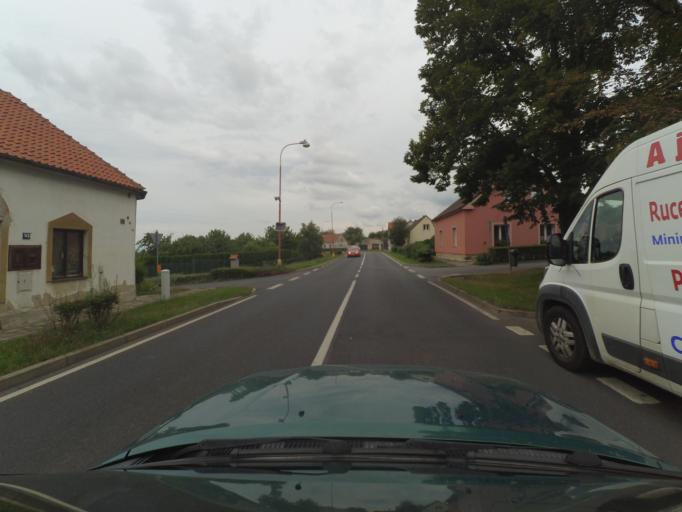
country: CZ
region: Ustecky
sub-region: Okres Louny
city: Louny
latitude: 50.3142
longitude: 13.8017
